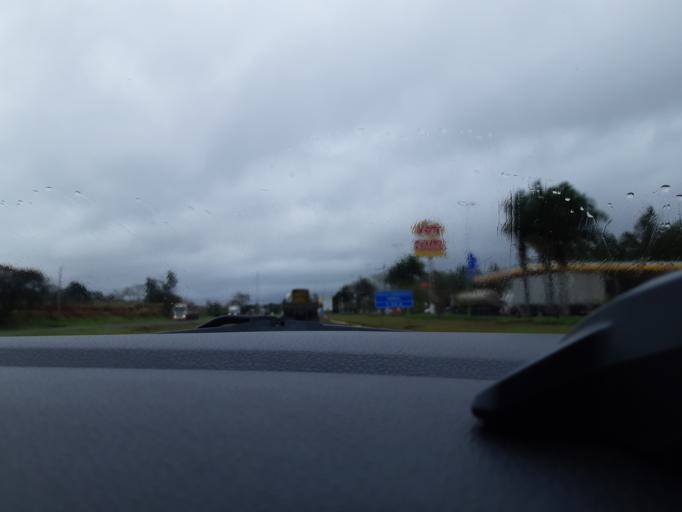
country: BR
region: Sao Paulo
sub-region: Ourinhos
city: Ourinhos
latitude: -22.9824
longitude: -49.9035
